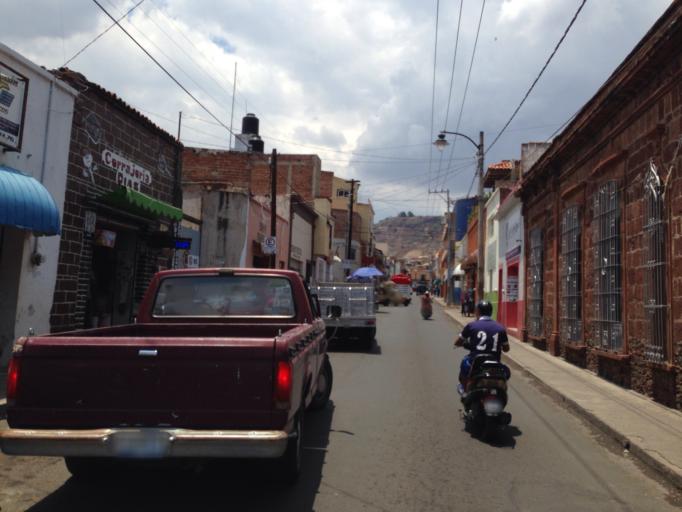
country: MX
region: Jalisco
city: Atotonilco el Alto
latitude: 20.5496
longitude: -102.5100
